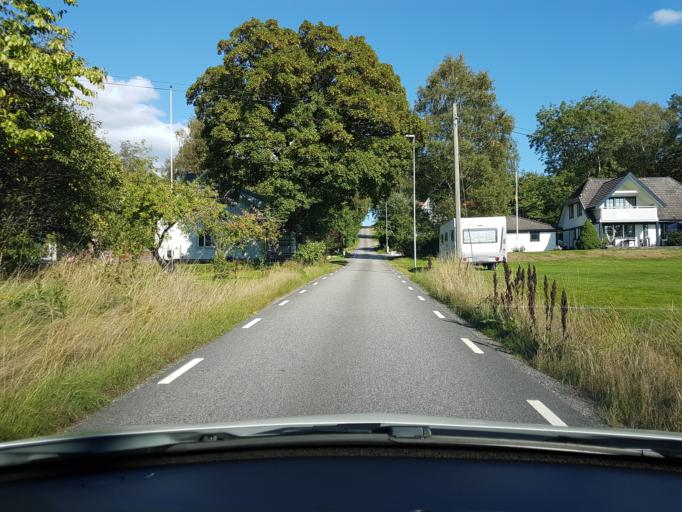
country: SE
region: Vaestra Goetaland
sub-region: Ale Kommun
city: Skepplanda
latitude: 57.9853
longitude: 12.2072
